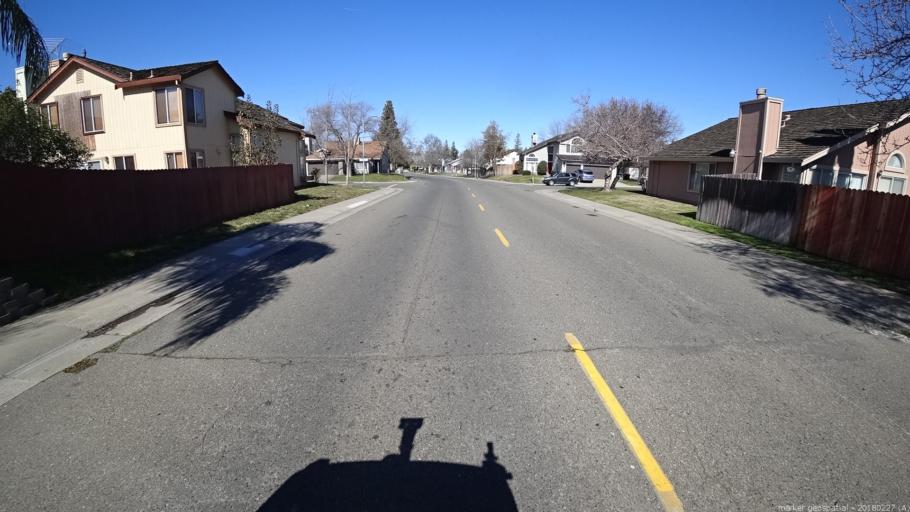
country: US
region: California
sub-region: Sacramento County
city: North Highlands
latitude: 38.7215
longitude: -121.3767
